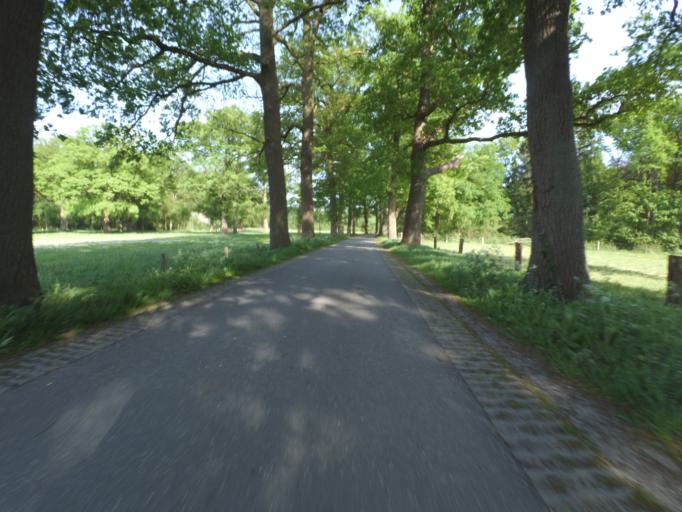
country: NL
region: Overijssel
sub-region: Gemeente Oldenzaal
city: Oldenzaal
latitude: 52.3793
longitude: 6.9714
